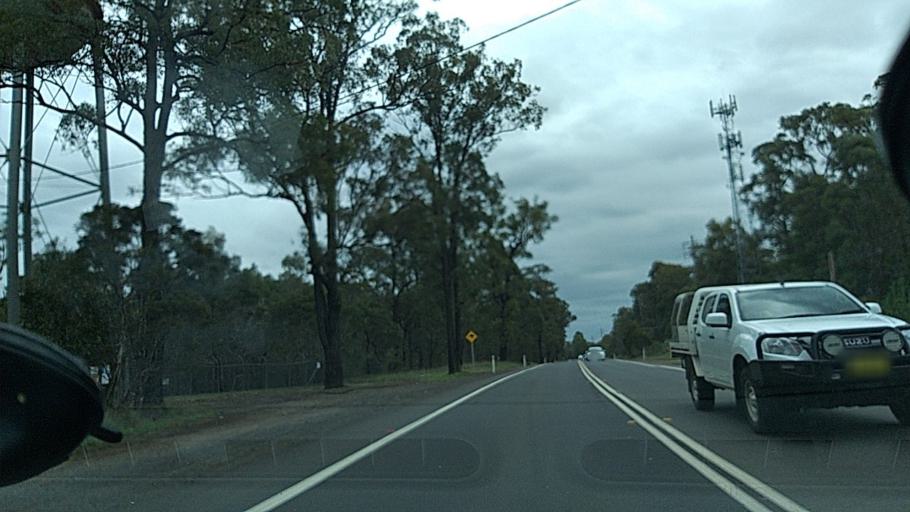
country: AU
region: New South Wales
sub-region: Hawkesbury
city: South Windsor
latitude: -33.6620
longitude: 150.7619
